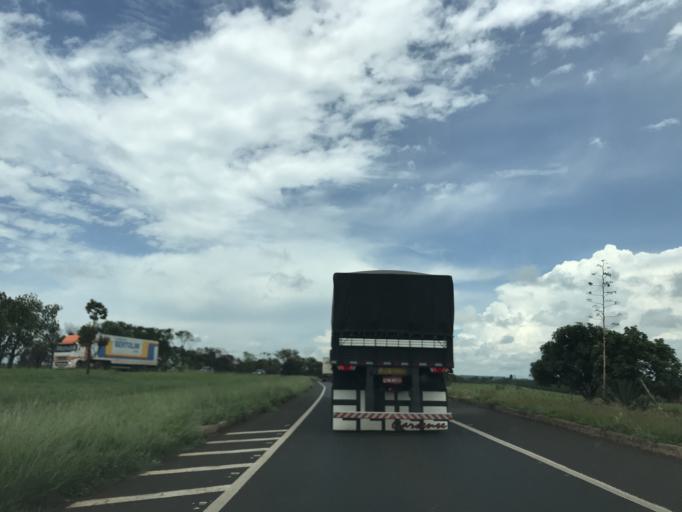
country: BR
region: Minas Gerais
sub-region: Frutal
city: Frutal
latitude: -19.7265
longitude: -48.9743
